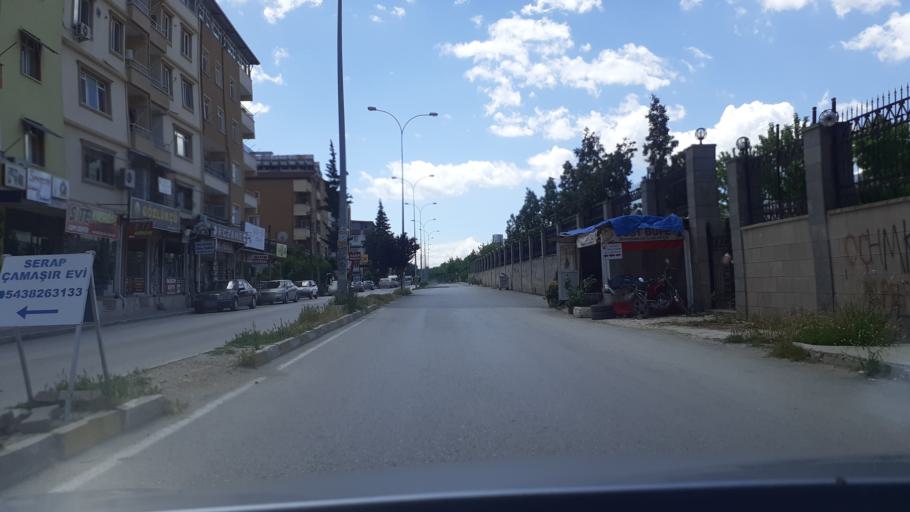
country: TR
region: Hatay
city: Anayazi
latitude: 36.3378
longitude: 36.2004
